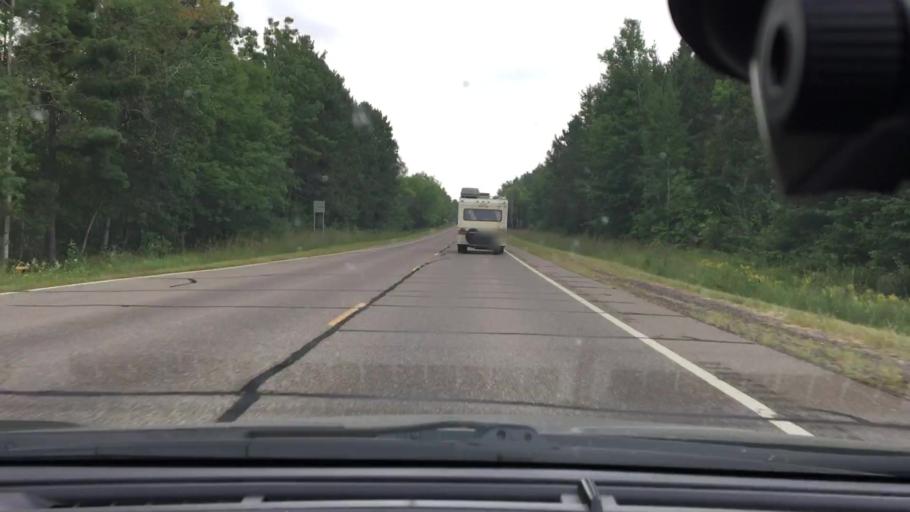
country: US
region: Minnesota
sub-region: Crow Wing County
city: Crosby
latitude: 46.4409
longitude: -93.8768
